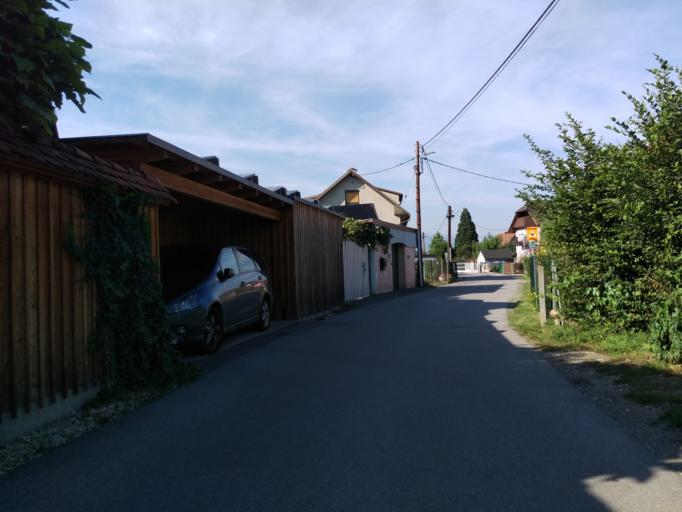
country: AT
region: Styria
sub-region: Politischer Bezirk Graz-Umgebung
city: Feldkirchen bei Graz
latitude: 47.0166
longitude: 15.4279
